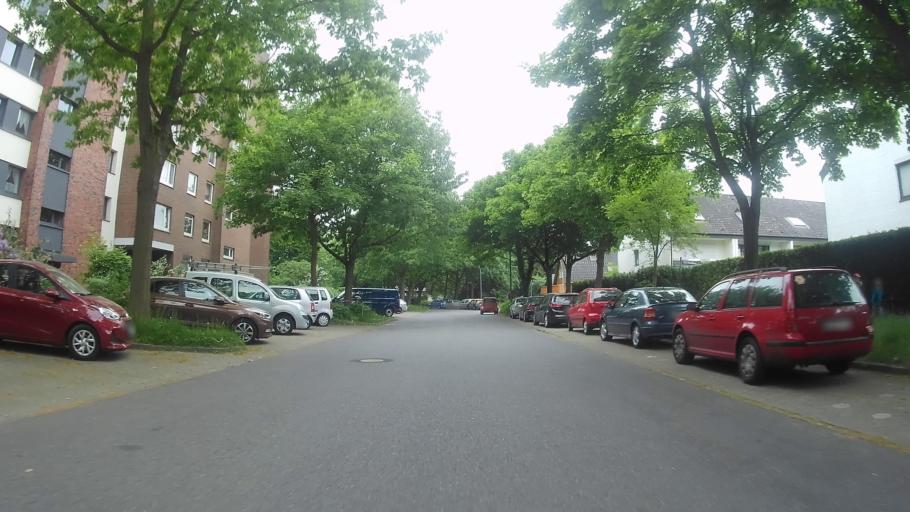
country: DE
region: Hamburg
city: Steilshoop
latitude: 53.6177
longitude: 10.0648
